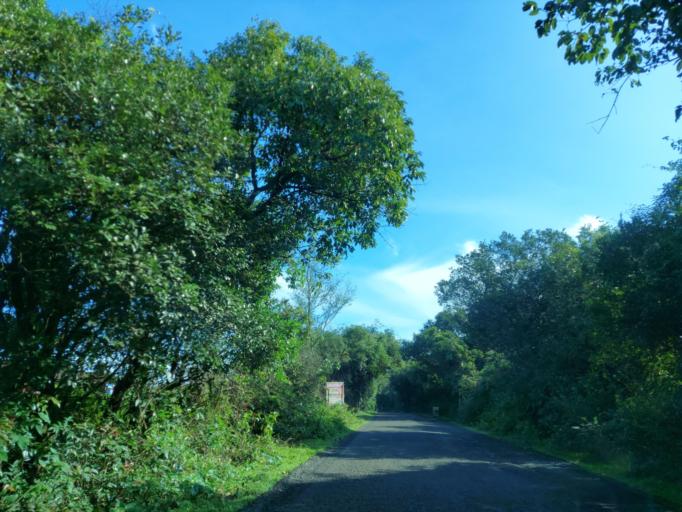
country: IN
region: Maharashtra
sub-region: Kolhapur
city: Ajra
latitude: 16.0236
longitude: 74.0557
